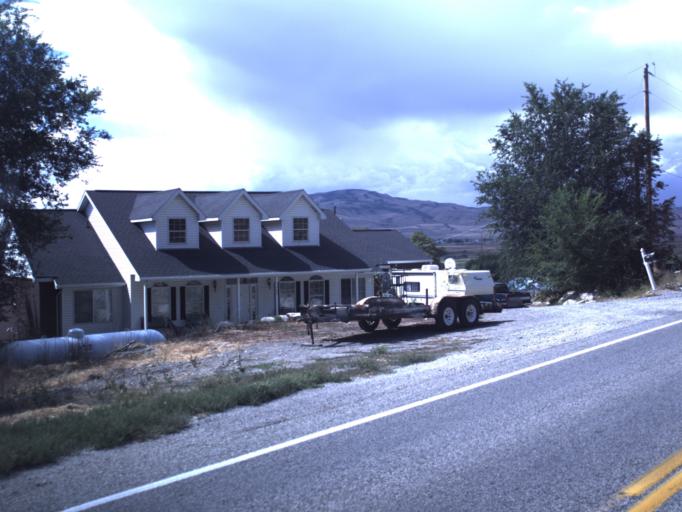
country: US
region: Utah
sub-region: Box Elder County
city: Elwood
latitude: 41.7236
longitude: -112.0954
